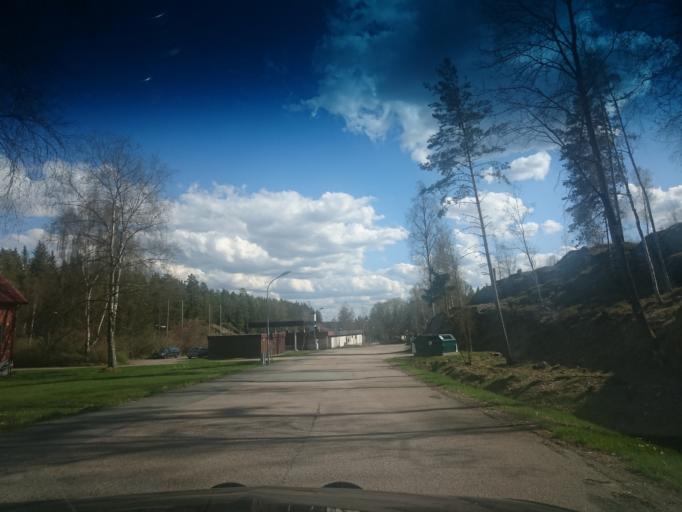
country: SE
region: Kronoberg
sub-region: Vaxjo Kommun
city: Braas
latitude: 57.2218
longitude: 15.1437
